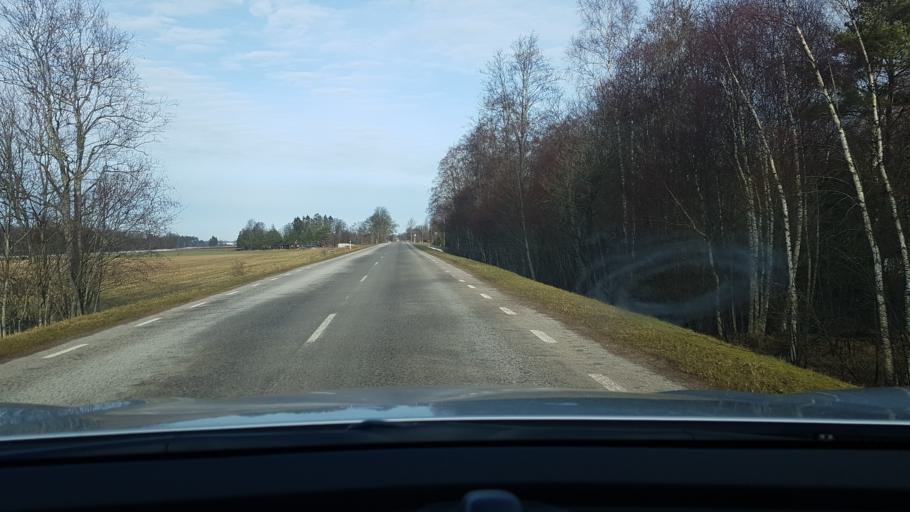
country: EE
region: Saare
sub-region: Kuressaare linn
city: Kuressaare
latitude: 58.4941
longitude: 22.7080
